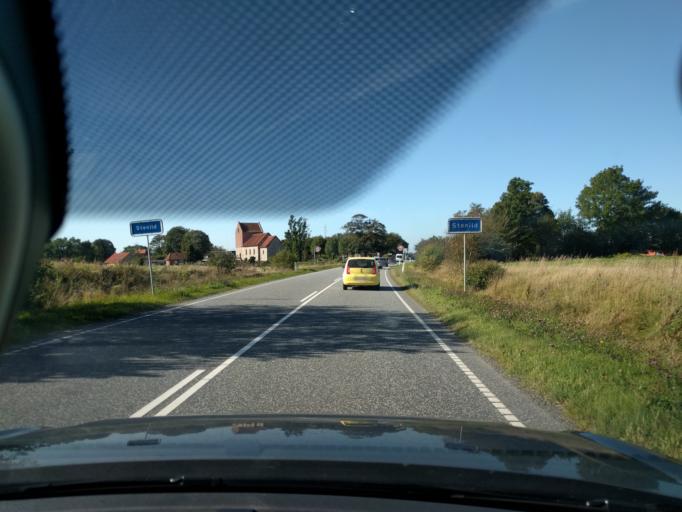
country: DK
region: North Denmark
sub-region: Mariagerfjord Kommune
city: Hobro
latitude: 56.6738
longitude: 9.6797
